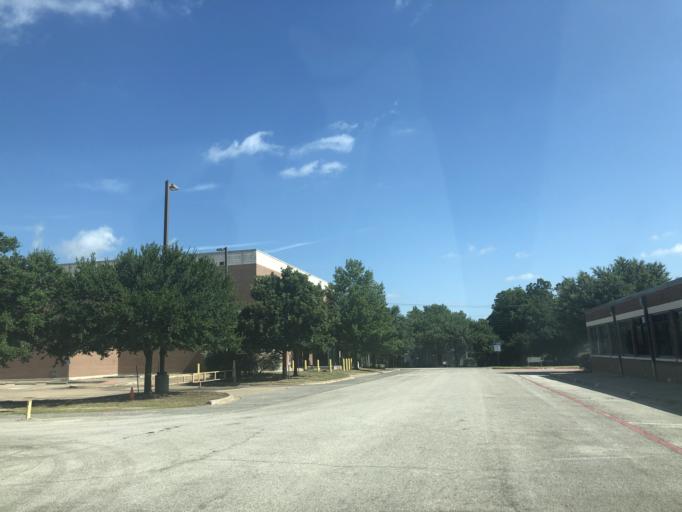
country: US
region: Texas
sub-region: Dallas County
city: Duncanville
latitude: 32.6502
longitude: -96.9060
